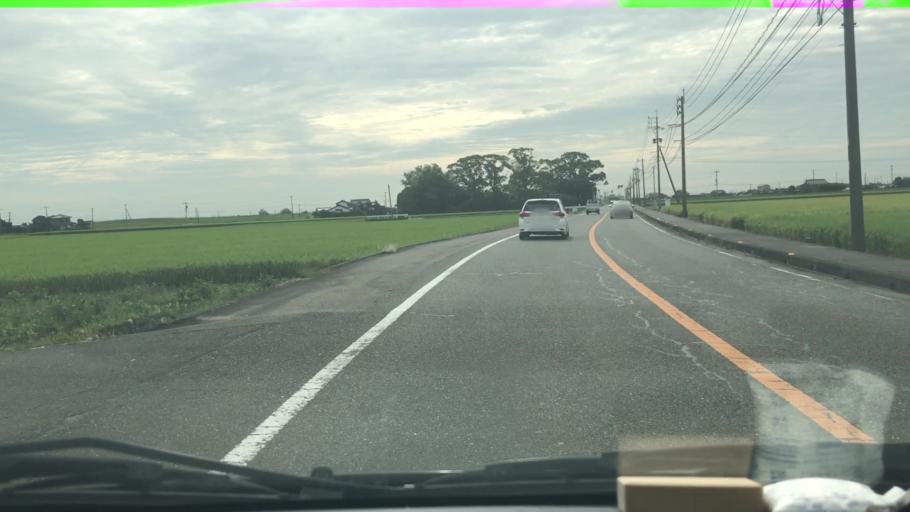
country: JP
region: Saga Prefecture
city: Takeocho-takeo
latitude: 33.2048
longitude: 130.0920
